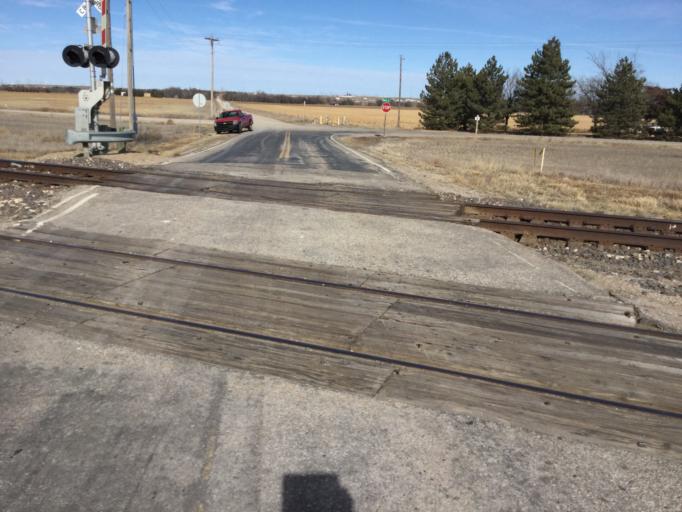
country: US
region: Kansas
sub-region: Ellis County
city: Hays
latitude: 38.8904
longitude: -99.3727
